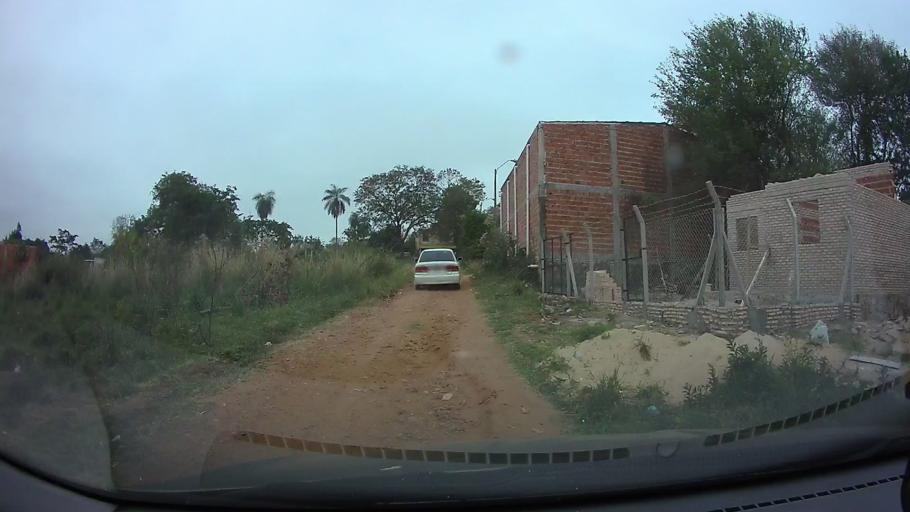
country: PY
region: Central
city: Limpio
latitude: -25.1546
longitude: -57.4566
